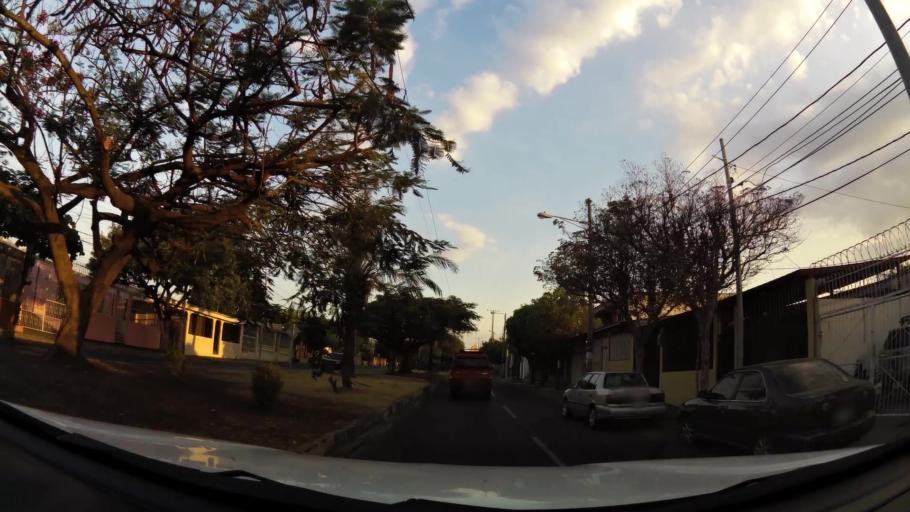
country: NI
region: Managua
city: Managua
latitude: 12.1487
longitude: -86.2343
